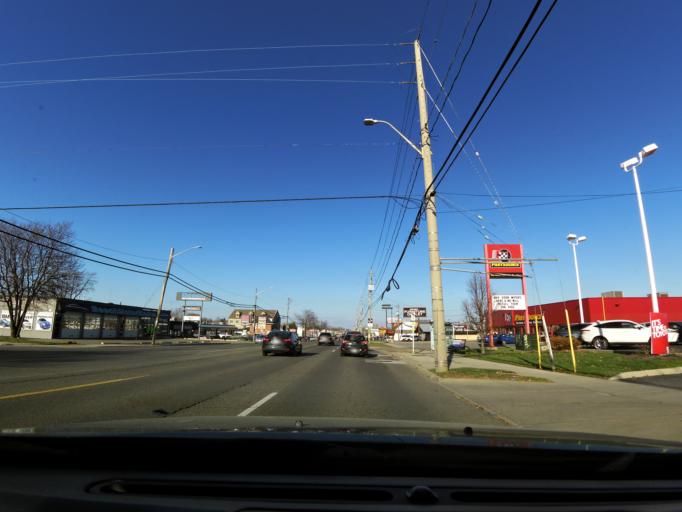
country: CA
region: Ontario
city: Hamilton
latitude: 43.2226
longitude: -79.8842
